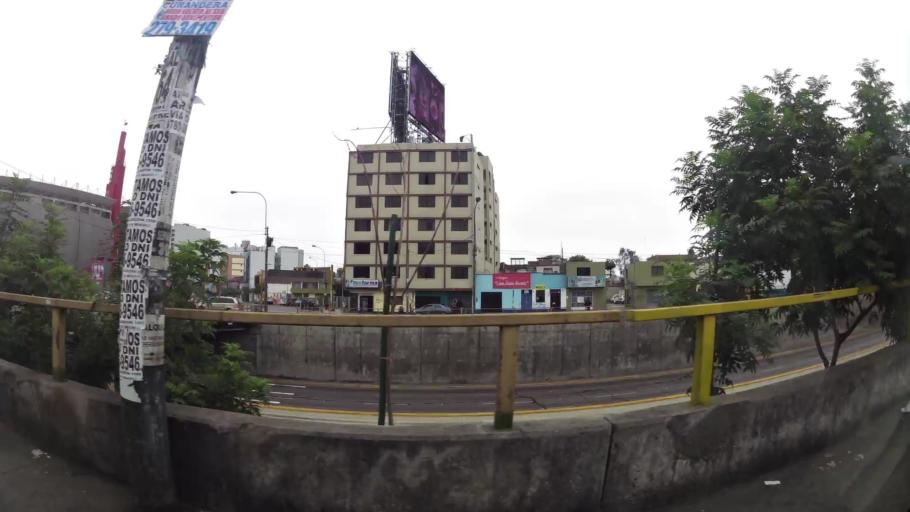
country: PE
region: Lima
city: Lima
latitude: -12.0647
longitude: -77.0334
